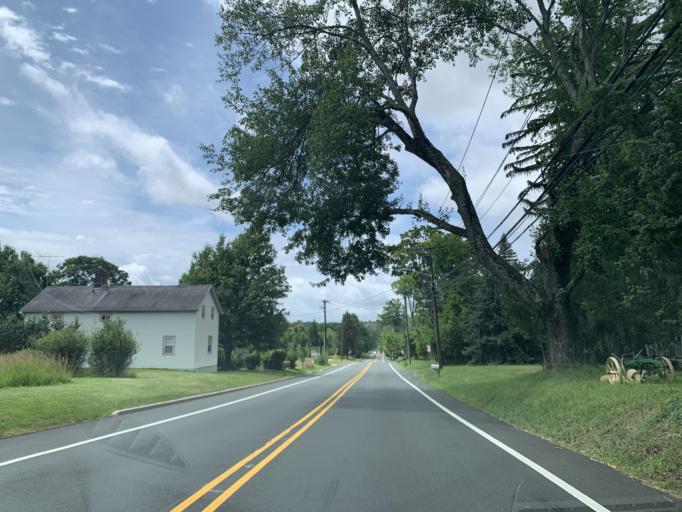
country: US
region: New Jersey
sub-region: Somerset County
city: Martinsville
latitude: 40.5993
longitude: -74.5599
